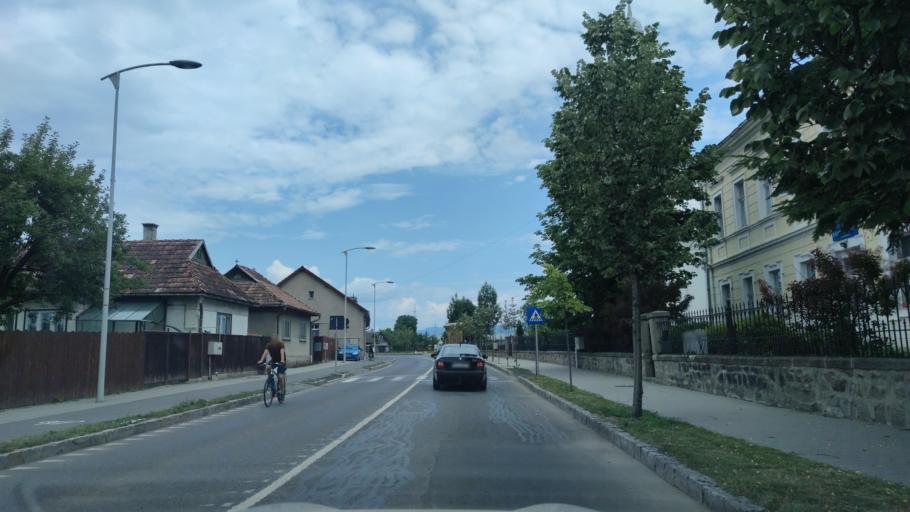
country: RO
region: Harghita
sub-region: Municipiul Miercurea Ciuc
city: Miercurea-Ciuc
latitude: 46.3776
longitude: 25.8012
